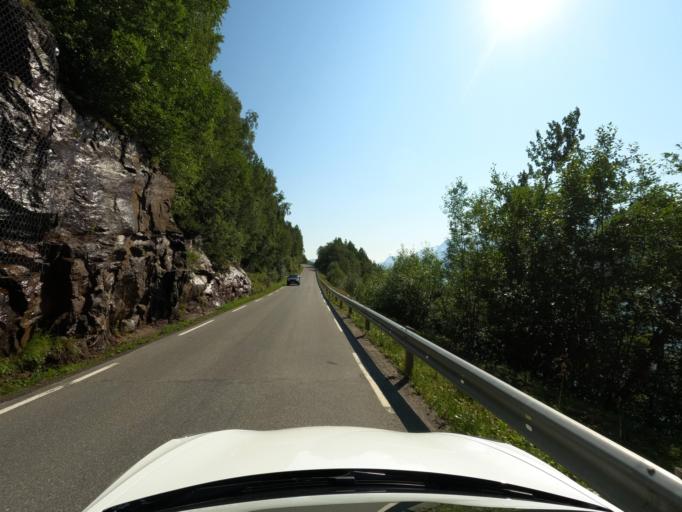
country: NO
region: Nordland
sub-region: Narvik
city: Narvik
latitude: 68.3620
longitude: 17.2622
